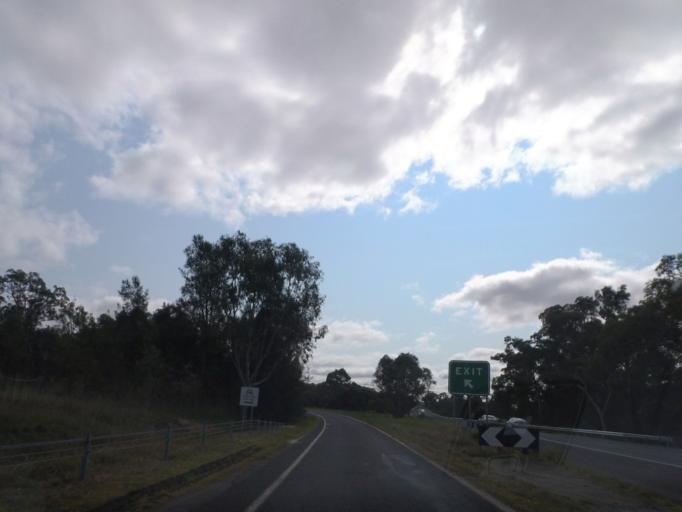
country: AU
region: Victoria
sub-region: Murrindindi
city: Kinglake West
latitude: -37.1116
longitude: 145.0916
